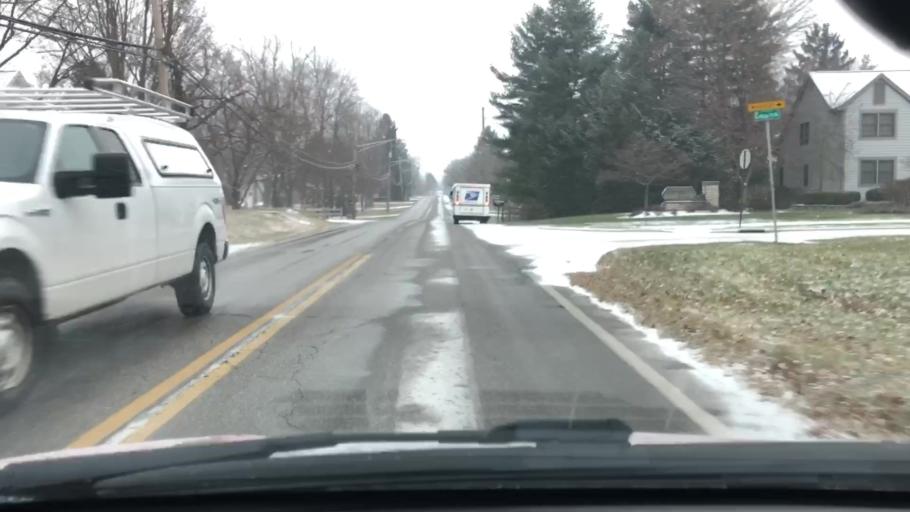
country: US
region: Ohio
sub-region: Franklin County
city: Westerville
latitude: 40.1257
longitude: -82.9120
